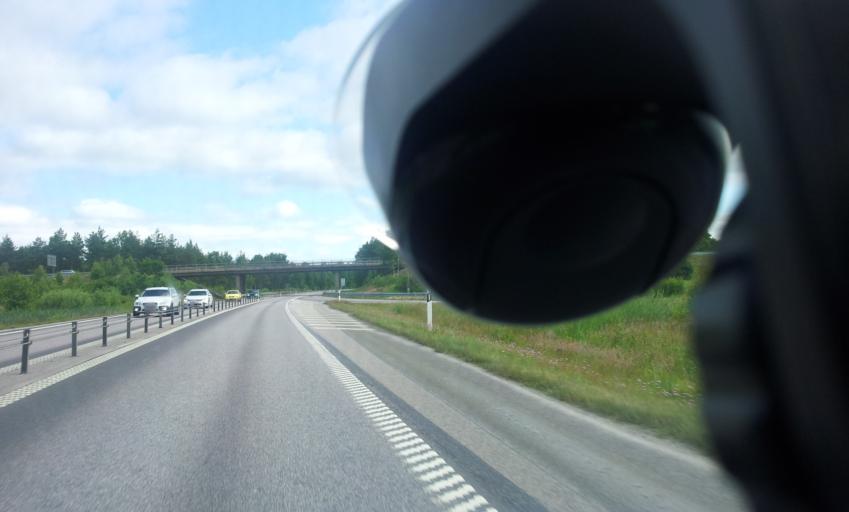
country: SE
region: Kalmar
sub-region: Kalmar Kommun
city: Lindsdal
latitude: 56.7568
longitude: 16.3081
